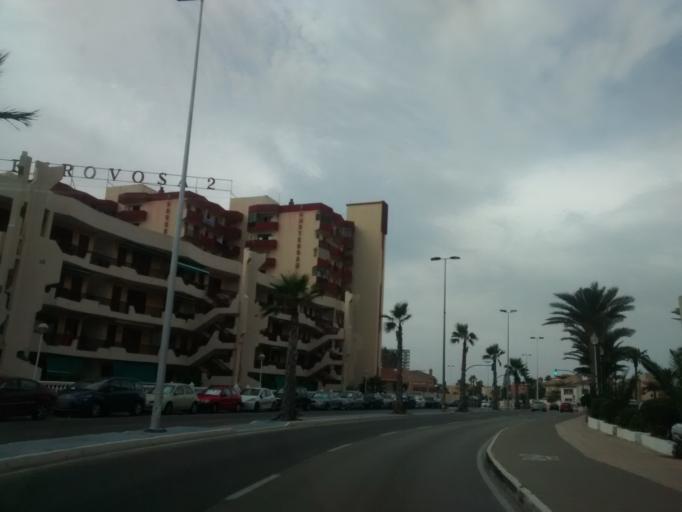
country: ES
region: Murcia
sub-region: Murcia
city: La Manga del Mar Menor
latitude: 37.6812
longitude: -0.7347
